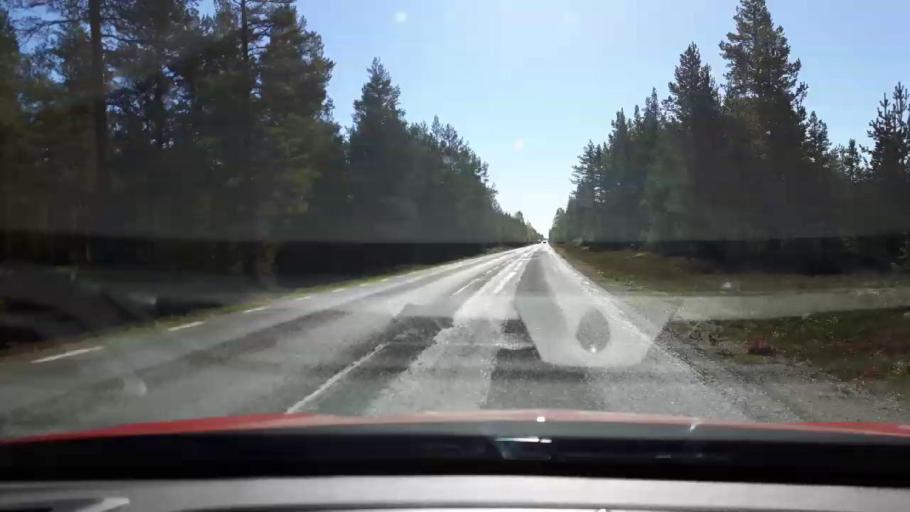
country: SE
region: Jaemtland
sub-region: Harjedalens Kommun
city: Sveg
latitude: 62.4216
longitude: 13.9066
